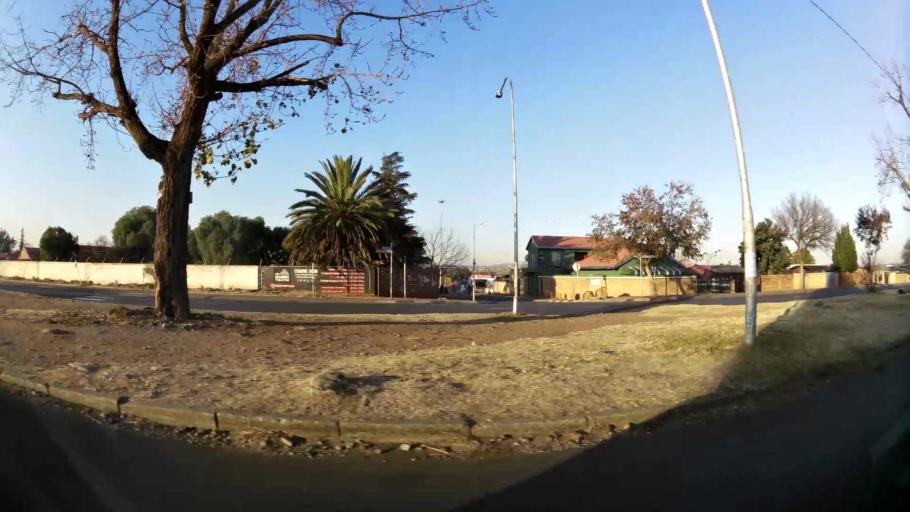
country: ZA
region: Gauteng
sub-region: City of Johannesburg Metropolitan Municipality
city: Soweto
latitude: -26.2485
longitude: 27.8834
